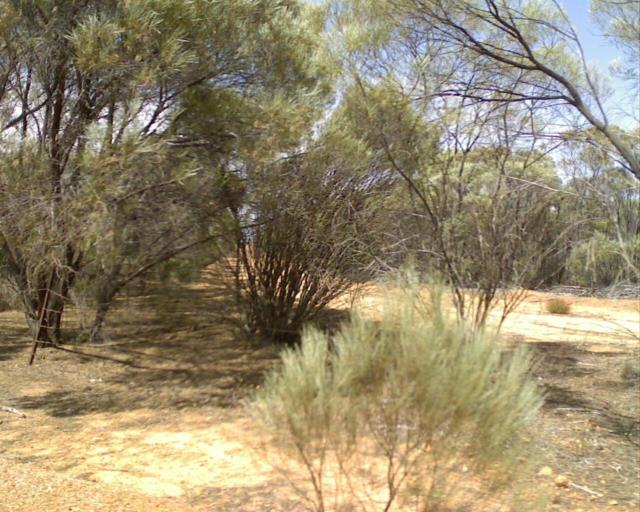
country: AU
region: Western Australia
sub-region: Merredin
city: Merredin
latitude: -30.9934
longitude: 118.3865
